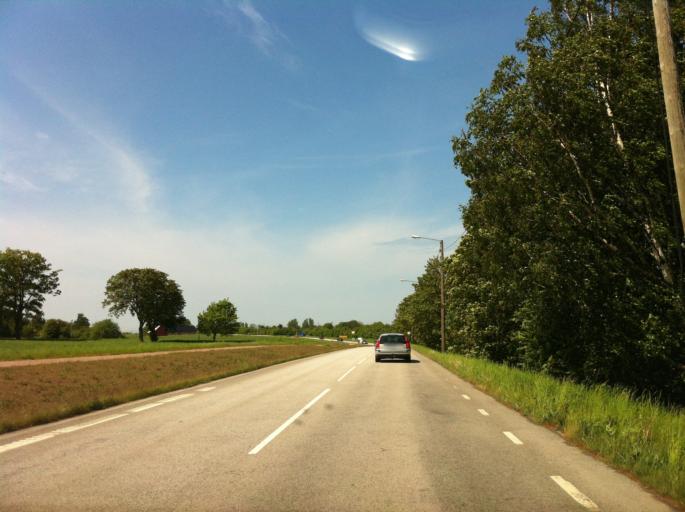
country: SE
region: Skane
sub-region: Helsingborg
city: Glumslov
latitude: 55.9248
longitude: 12.8429
